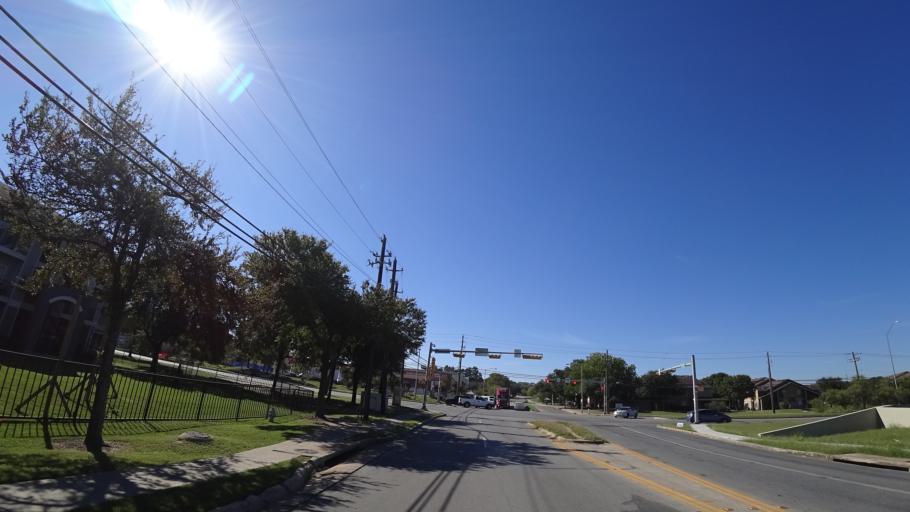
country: US
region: Texas
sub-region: Travis County
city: Austin
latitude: 30.2328
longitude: -97.7202
